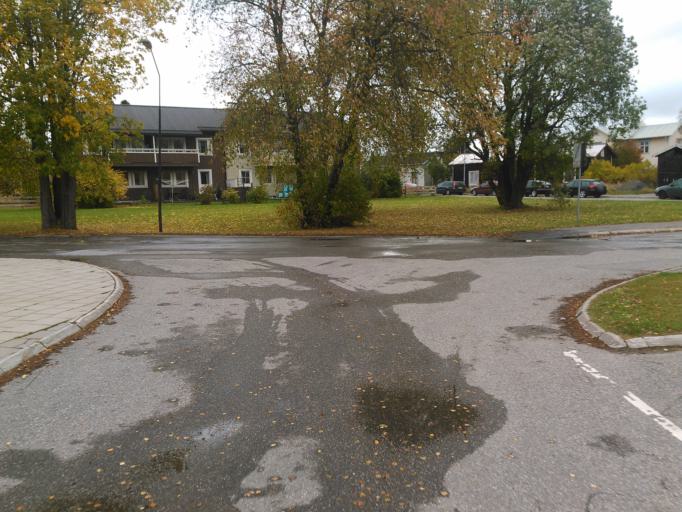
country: SE
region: Vaesterbotten
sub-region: Umea Kommun
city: Umea
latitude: 63.8200
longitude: 20.2465
